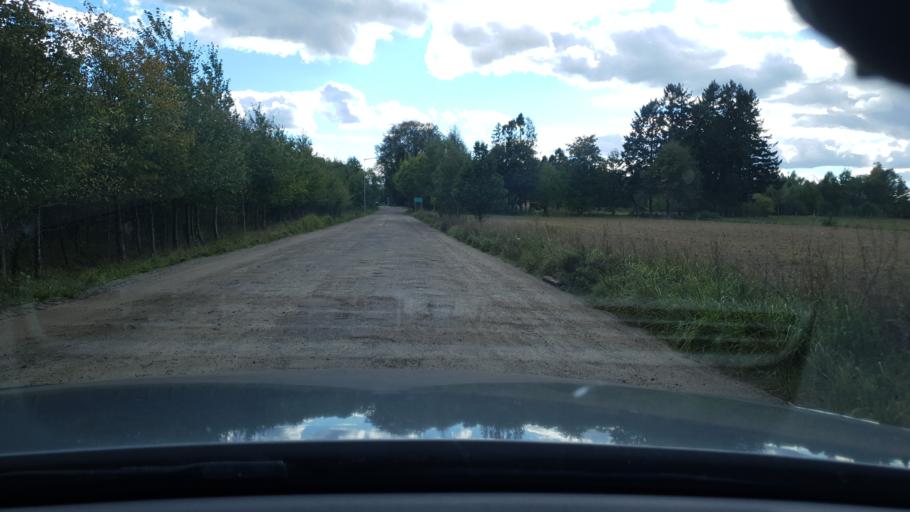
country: PL
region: Pomeranian Voivodeship
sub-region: Powiat wejherowski
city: Reda
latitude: 54.5815
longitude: 18.3130
